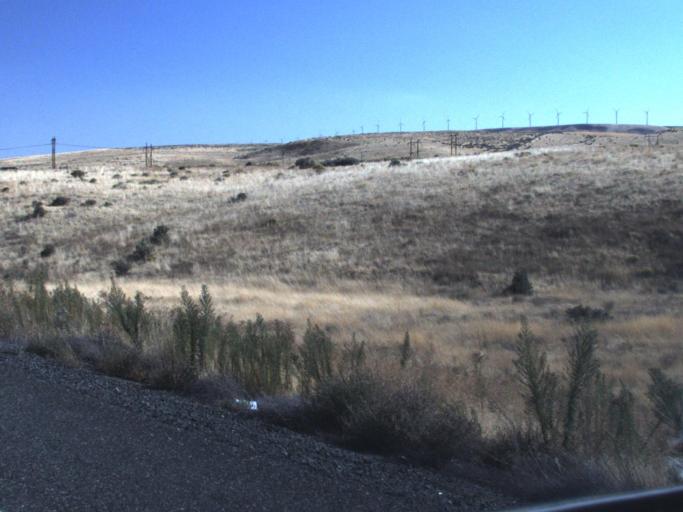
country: US
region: Washington
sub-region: Benton County
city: Highland
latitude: 46.1480
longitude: -119.1204
